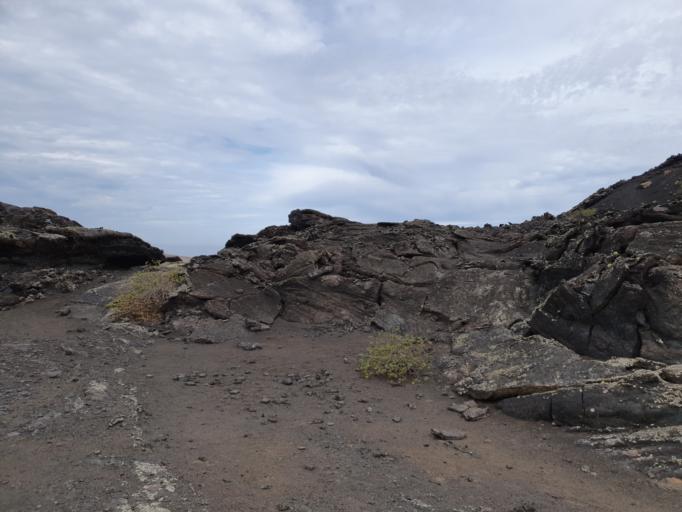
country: ES
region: Canary Islands
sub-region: Provincia de Las Palmas
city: Tinajo
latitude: 29.0111
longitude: -13.7182
